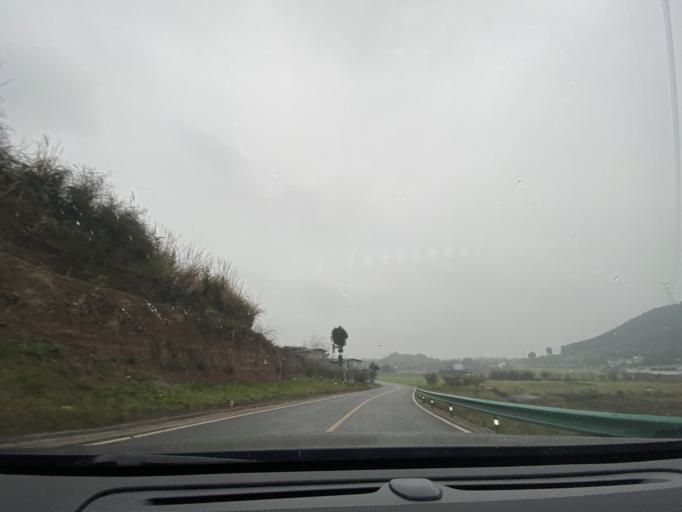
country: CN
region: Sichuan
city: Jiancheng
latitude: 30.3908
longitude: 104.6363
